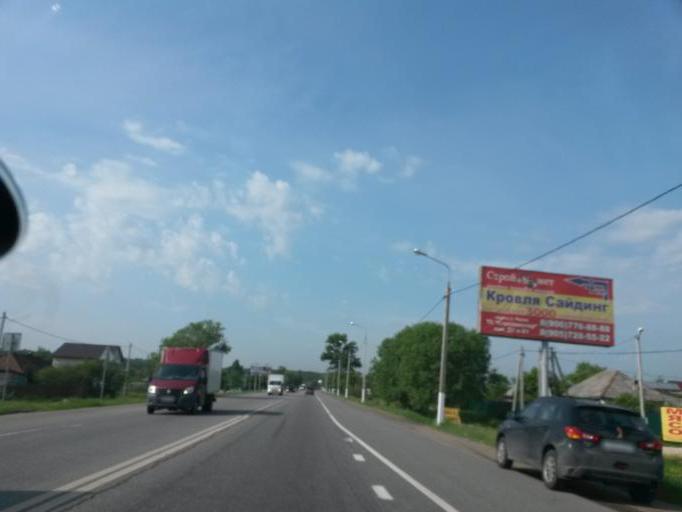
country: RU
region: Moskovskaya
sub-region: Chekhovskiy Rayon
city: Chekhov
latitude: 55.1869
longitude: 37.4981
